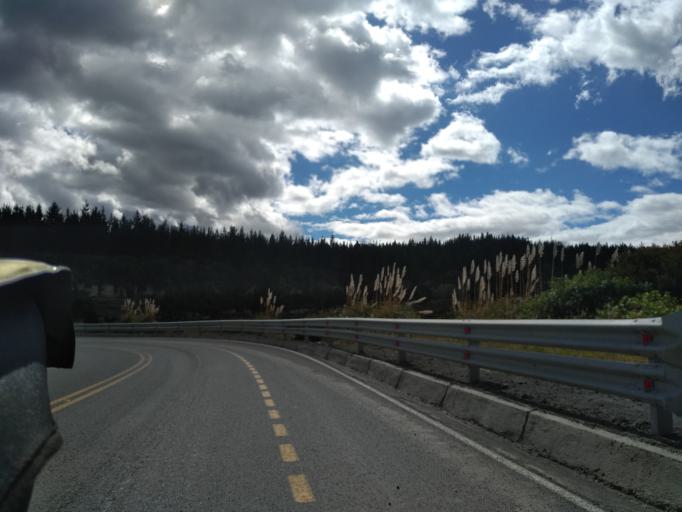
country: EC
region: Cotopaxi
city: Saquisili
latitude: -0.6919
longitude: -78.5681
